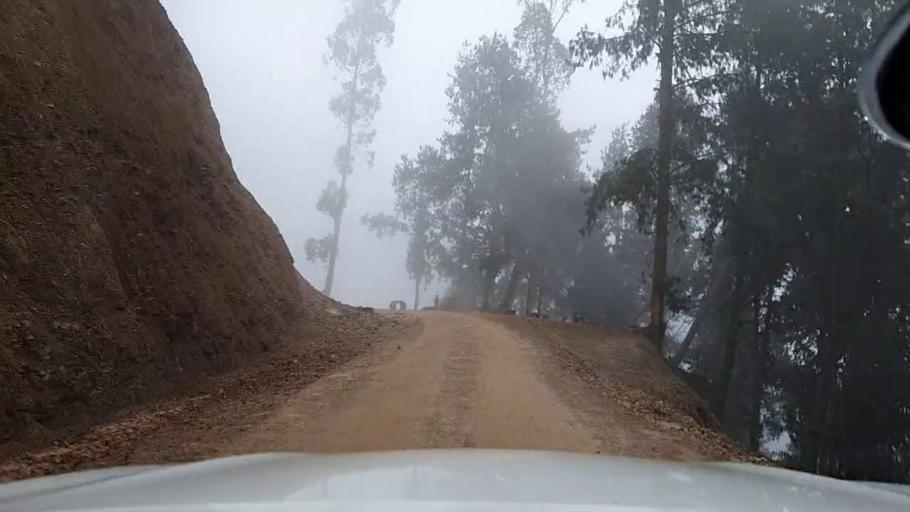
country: BI
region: Cibitoke
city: Cibitoke
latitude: -2.5994
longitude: 29.1951
